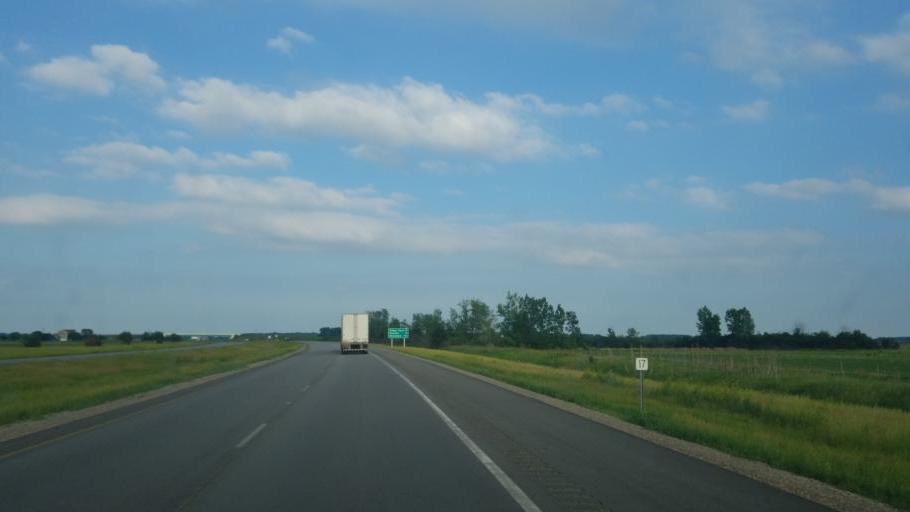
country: US
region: Ohio
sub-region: Van Wert County
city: Van Wert
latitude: 40.8707
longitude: -84.5132
